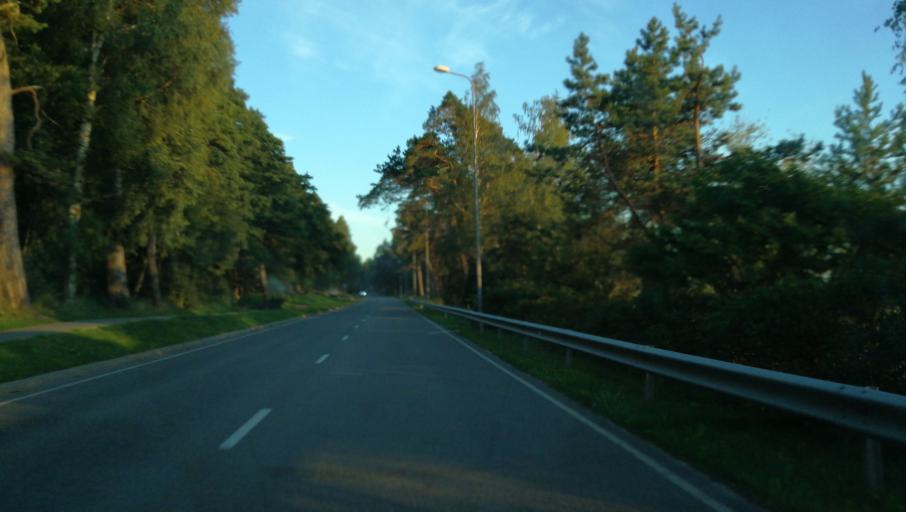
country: LV
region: Saulkrastu
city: Saulkrasti
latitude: 57.2873
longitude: 24.4130
